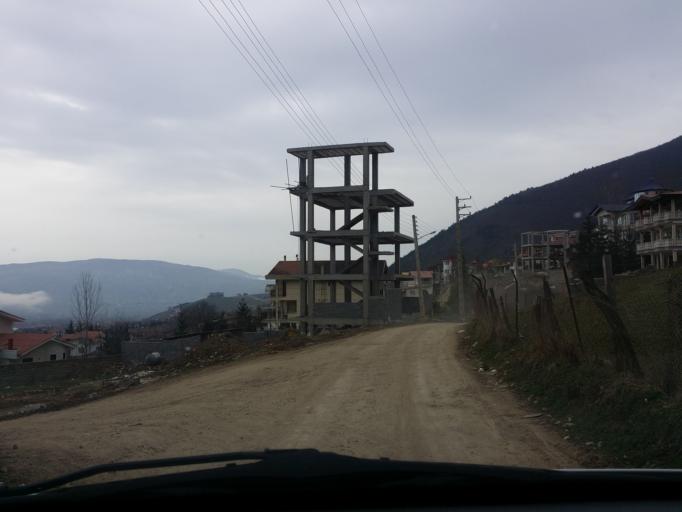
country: IR
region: Mazandaran
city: `Abbasabad
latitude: 36.4923
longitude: 51.1570
